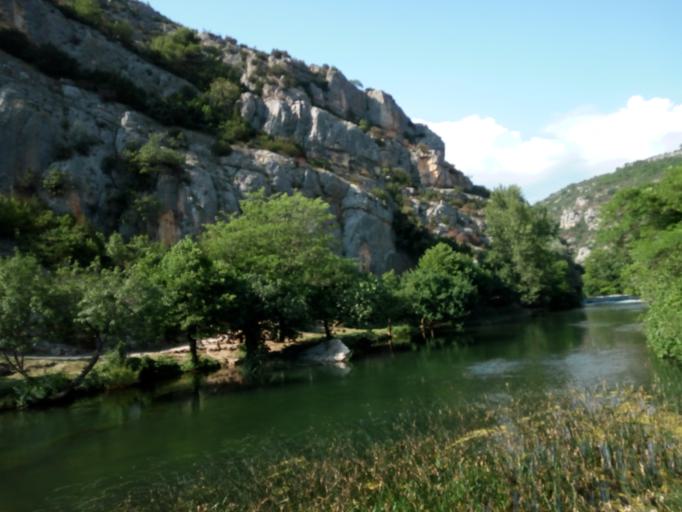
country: HR
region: Sibensko-Kniniska
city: Kistanje
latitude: 43.9061
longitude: 15.9753
